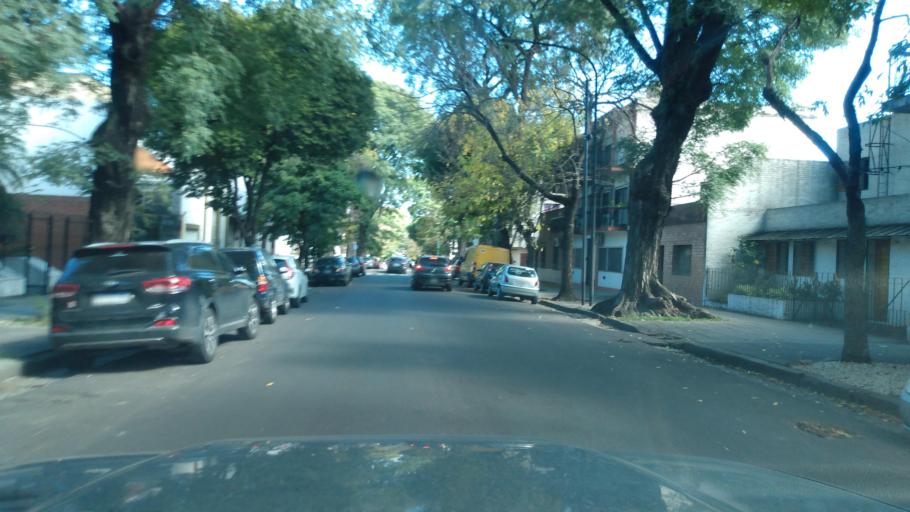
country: AR
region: Buenos Aires
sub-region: Partido de General San Martin
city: General San Martin
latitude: -34.5735
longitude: -58.4927
